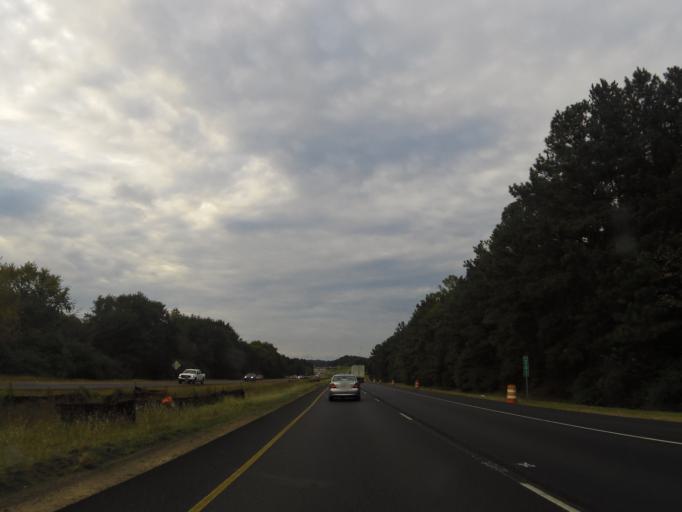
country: US
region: Alabama
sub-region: Shelby County
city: Pelham
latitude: 33.2677
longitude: -86.7991
